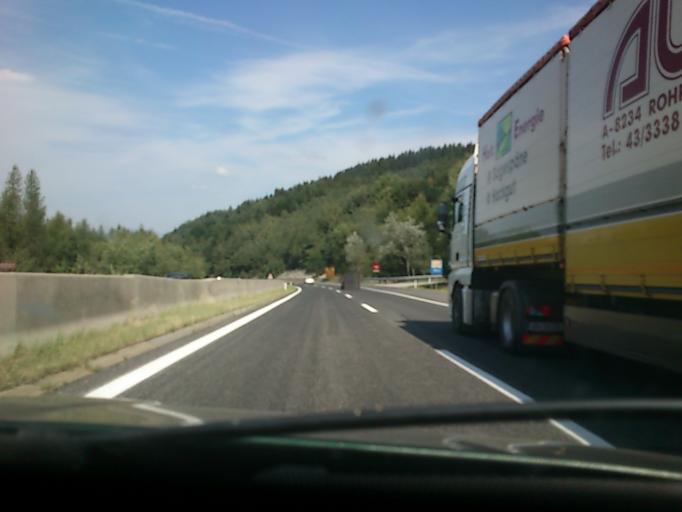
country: AT
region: Lower Austria
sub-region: Politischer Bezirk Neunkirchen
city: Thomasberg
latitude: 47.5608
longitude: 16.1218
